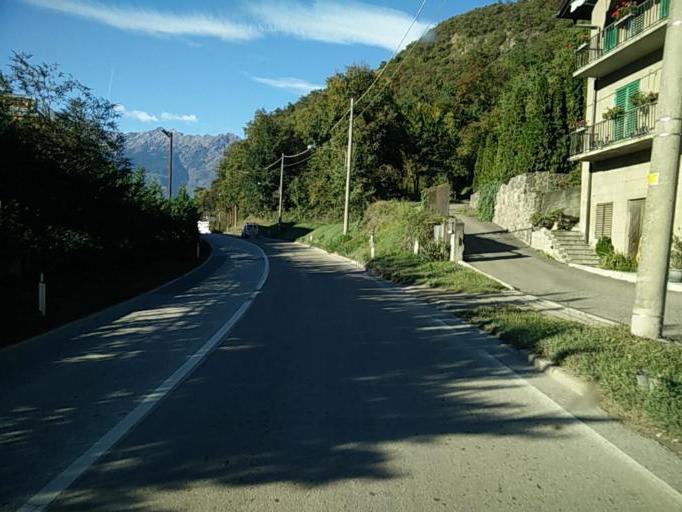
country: IT
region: Trentino-Alto Adige
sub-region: Bolzano
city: Sinigo
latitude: 46.6254
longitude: 11.1846
